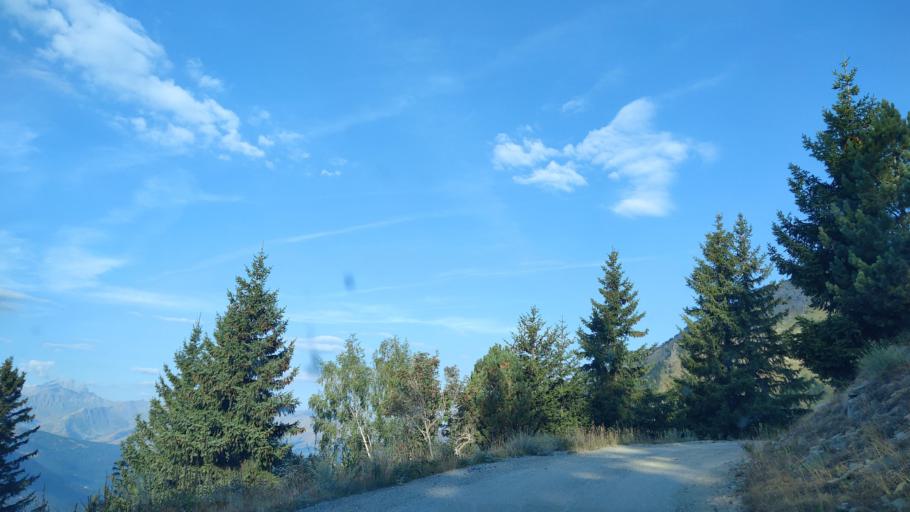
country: FR
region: Rhone-Alpes
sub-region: Departement de la Savoie
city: Val Thorens
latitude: 45.2277
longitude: 6.5619
